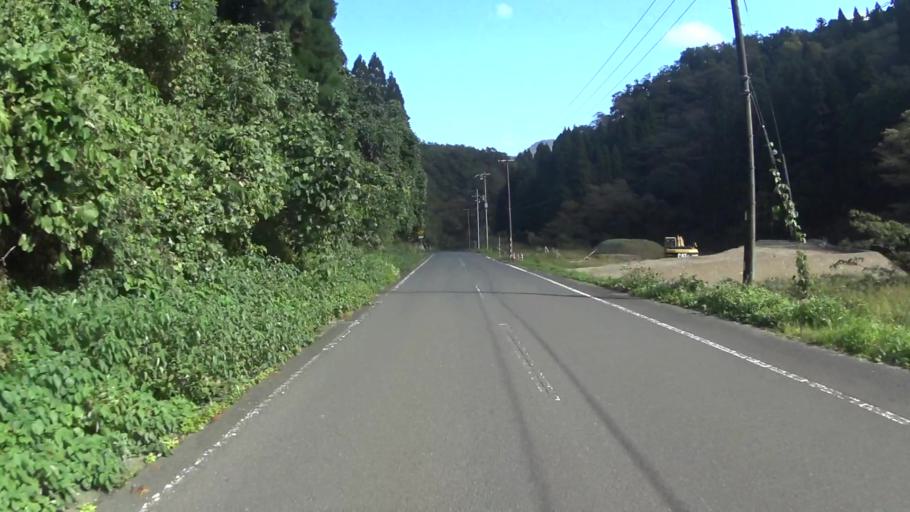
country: JP
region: Kyoto
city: Miyazu
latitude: 35.6327
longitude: 135.1234
